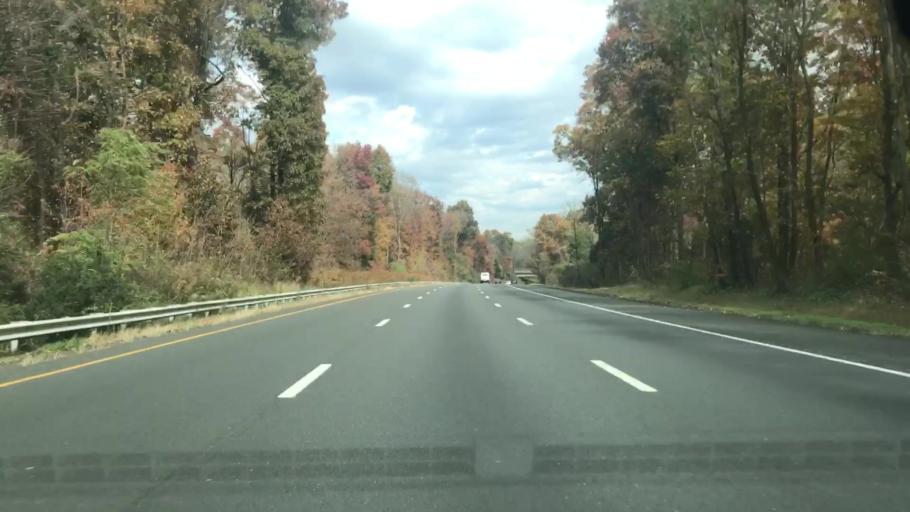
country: US
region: New Jersey
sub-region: Somerset County
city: Bernardsville
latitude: 40.7408
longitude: -74.5342
